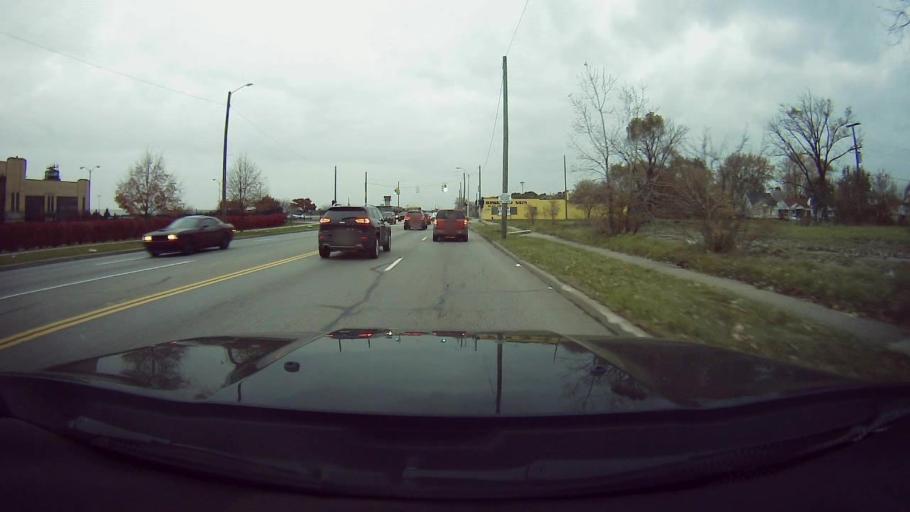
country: US
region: Michigan
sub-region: Wayne County
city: Hamtramck
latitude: 42.4067
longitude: -82.9996
